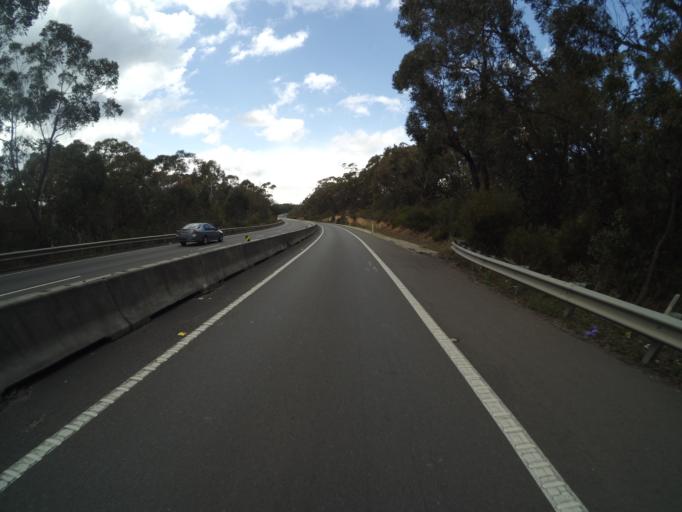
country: AU
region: New South Wales
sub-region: Wollongong
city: Mount Keira
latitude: -34.3484
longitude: 150.7986
